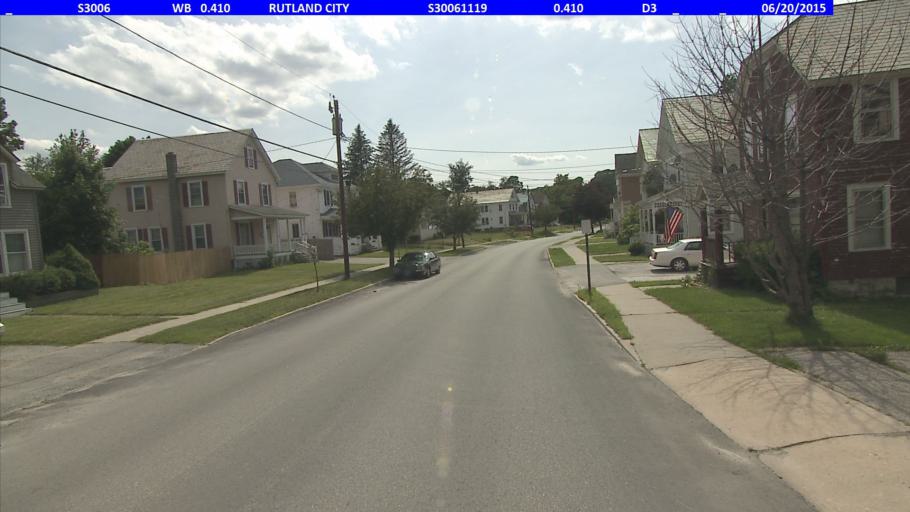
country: US
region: Vermont
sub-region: Rutland County
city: Rutland
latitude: 43.6152
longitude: -72.9838
